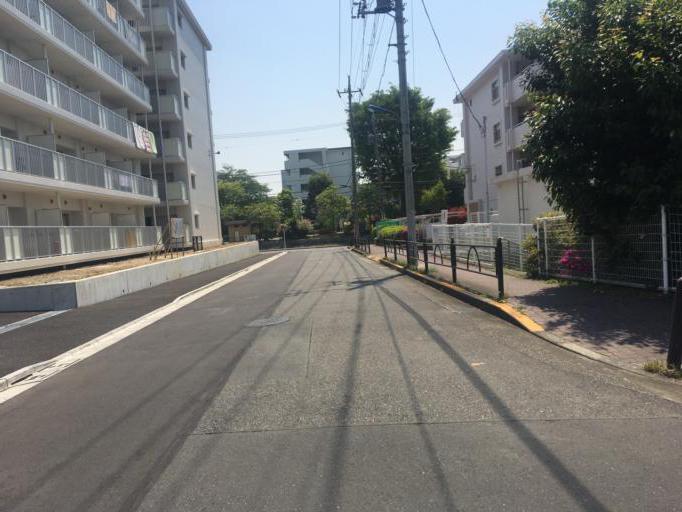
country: JP
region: Saitama
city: Wako
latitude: 35.7714
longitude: 139.6299
